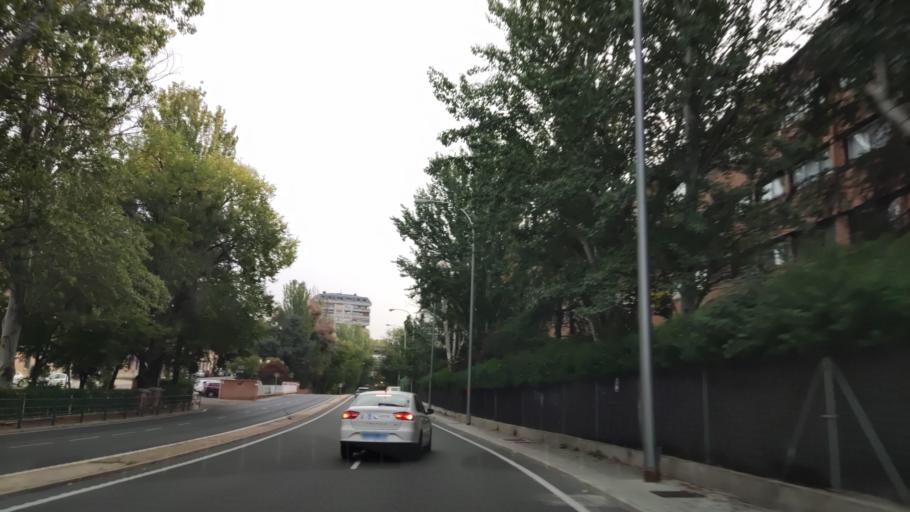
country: ES
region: Madrid
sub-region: Provincia de Madrid
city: Fuencarral-El Pardo
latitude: 40.4754
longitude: -3.7453
